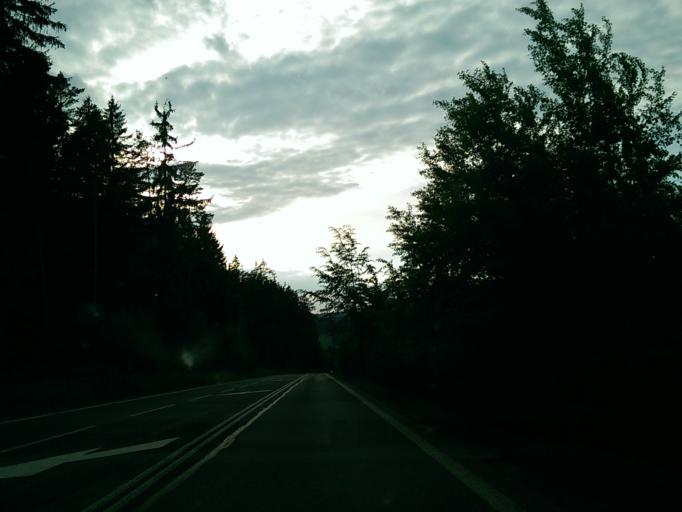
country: CZ
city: Plavy
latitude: 50.6836
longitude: 15.2797
